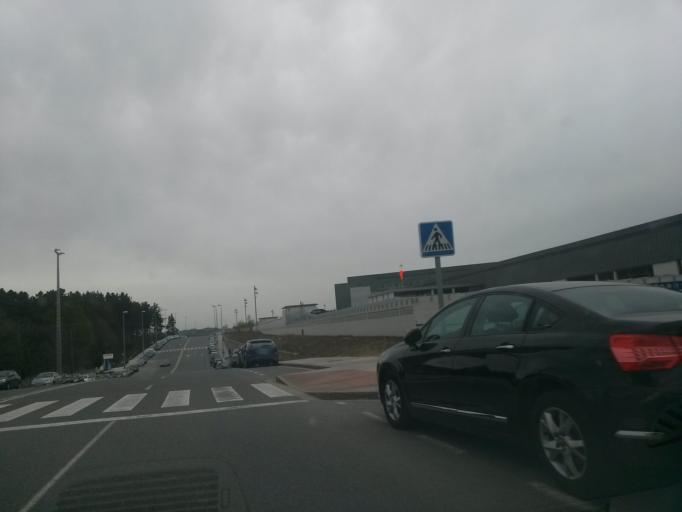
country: ES
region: Galicia
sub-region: Provincia de Lugo
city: Lugo
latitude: 43.0201
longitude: -7.5369
